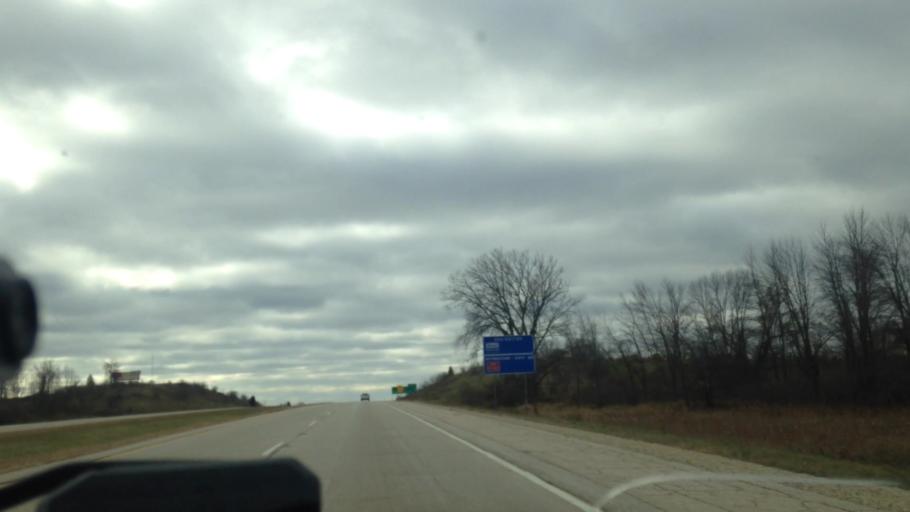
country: US
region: Wisconsin
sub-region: Washington County
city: Richfield
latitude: 43.2918
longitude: -88.1871
